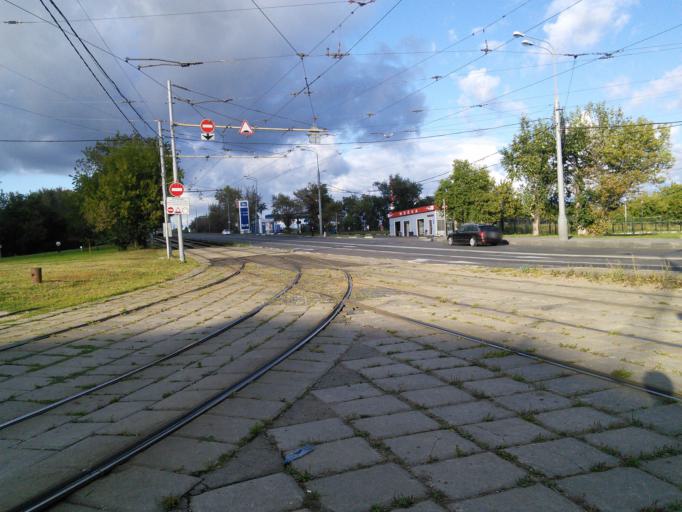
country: RU
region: Moskovskaya
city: Bogorodskoye
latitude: 55.8135
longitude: 37.7357
